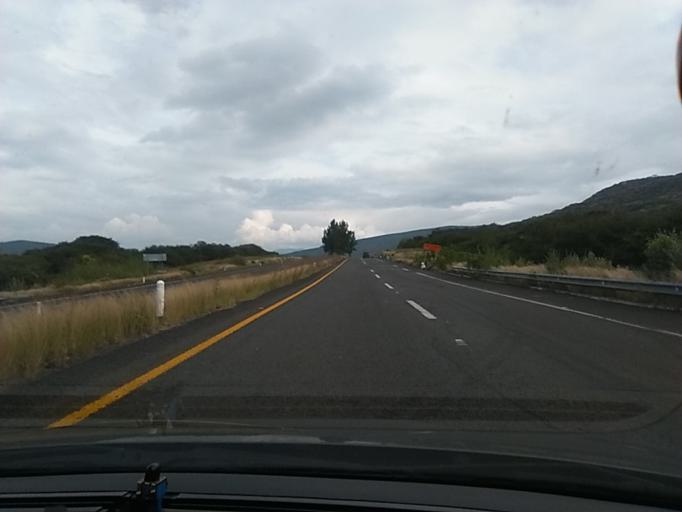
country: MX
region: Michoacan
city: Ixtlan
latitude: 20.2294
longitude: -102.3756
